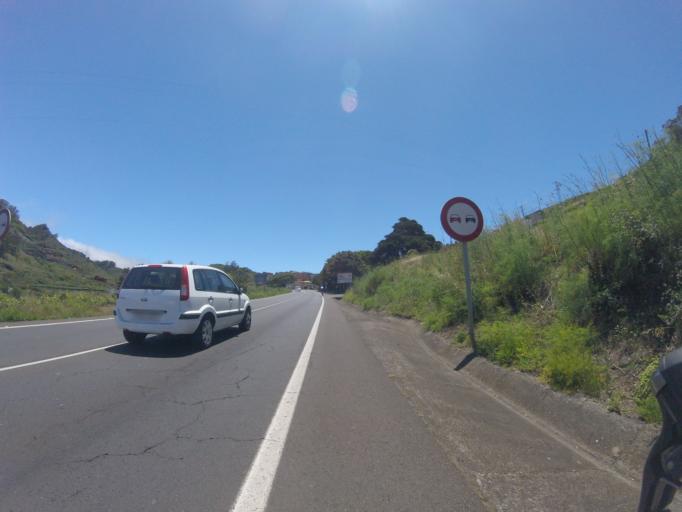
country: ES
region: Canary Islands
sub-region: Provincia de Santa Cruz de Tenerife
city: Tegueste
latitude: 28.5137
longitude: -16.3110
